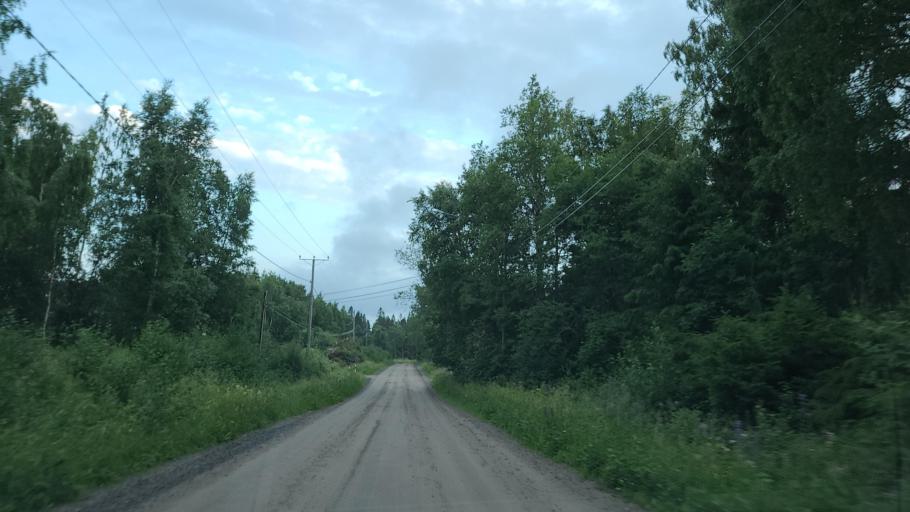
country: FI
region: Ostrobothnia
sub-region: Vaasa
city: Replot
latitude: 63.3120
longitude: 21.1594
